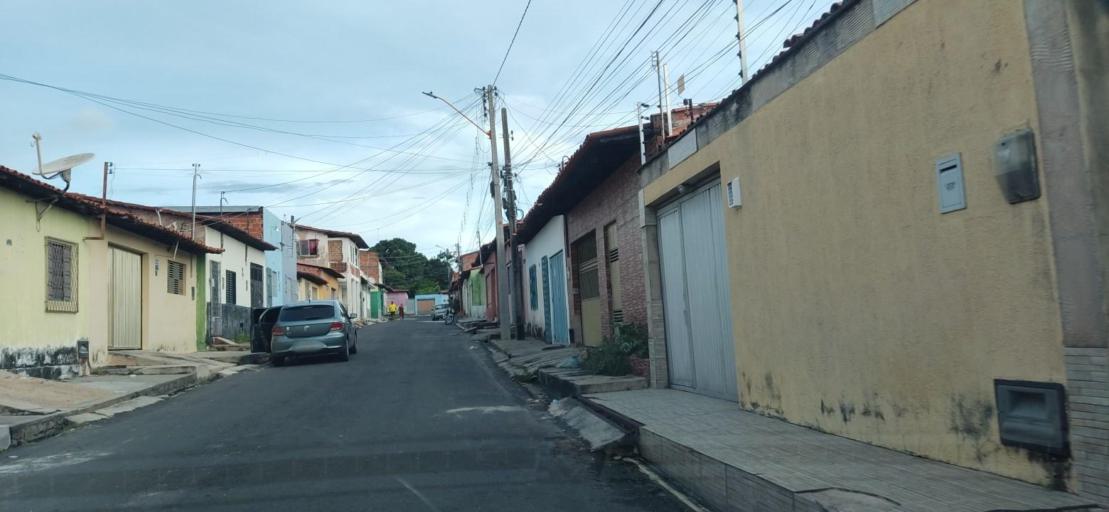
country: BR
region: Piaui
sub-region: Teresina
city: Teresina
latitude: -5.1524
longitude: -42.7867
